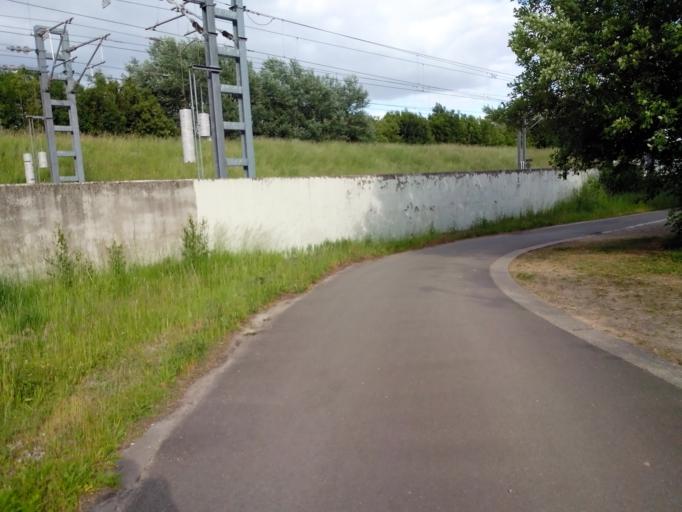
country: BE
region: Flanders
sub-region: Provincie Vlaams-Brabant
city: Bierbeek
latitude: 50.8516
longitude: 4.7366
